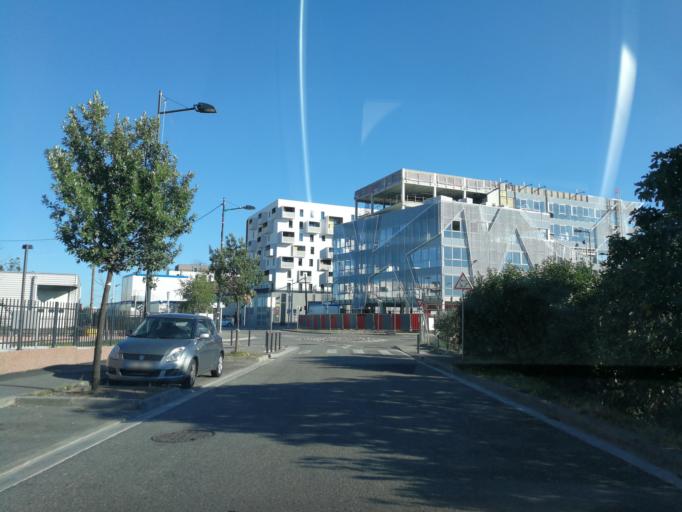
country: FR
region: Midi-Pyrenees
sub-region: Departement de la Haute-Garonne
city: L'Union
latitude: 43.6426
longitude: 1.4532
